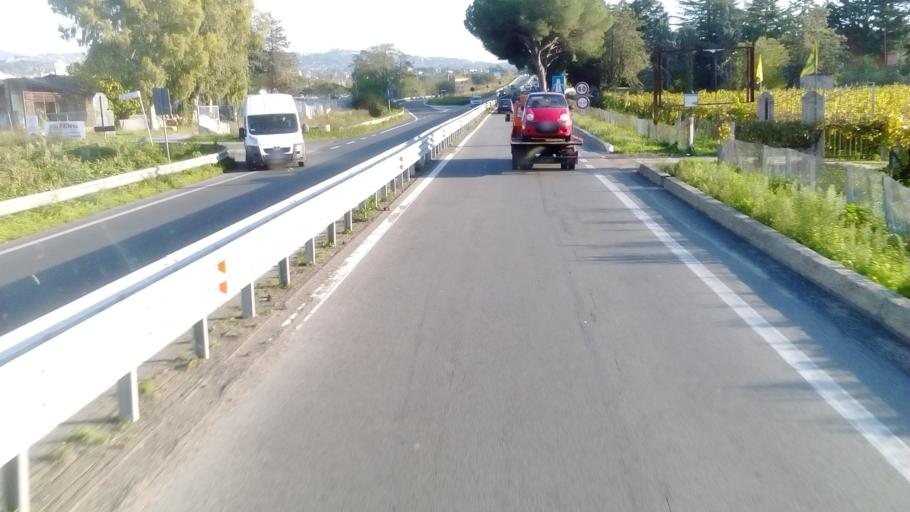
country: IT
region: Latium
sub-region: Citta metropolitana di Roma Capitale
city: Ciampino
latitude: 41.7811
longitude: 12.6030
